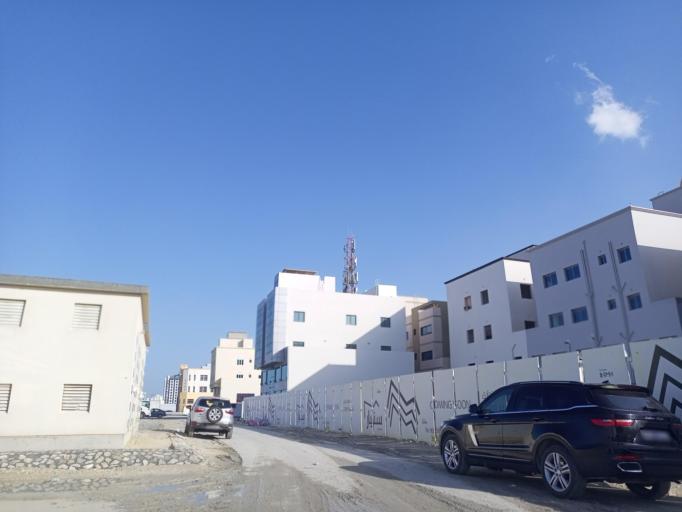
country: BH
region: Muharraq
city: Al Hadd
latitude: 26.2266
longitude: 50.6309
